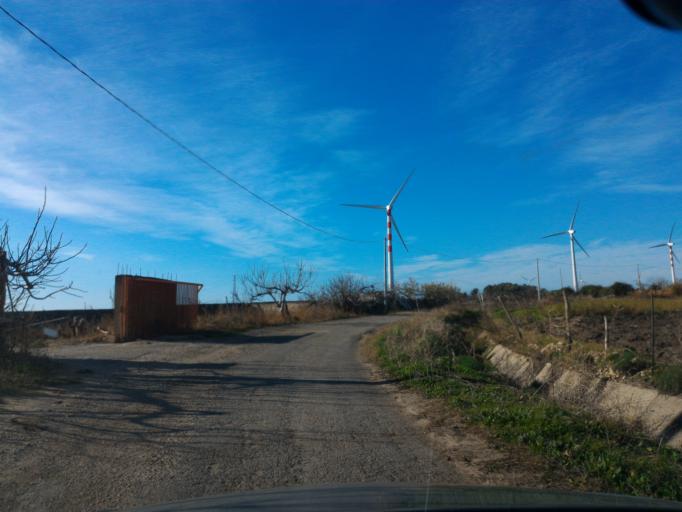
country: IT
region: Calabria
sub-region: Provincia di Crotone
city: Isola di Capo Rizzuto
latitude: 38.9448
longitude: 17.0553
